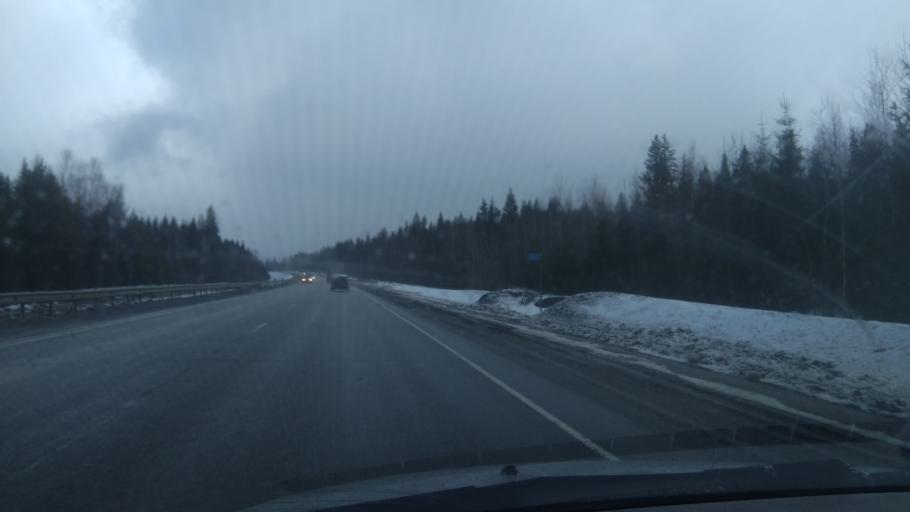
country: RU
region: Sverdlovsk
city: Arti
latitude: 56.7887
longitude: 58.5059
